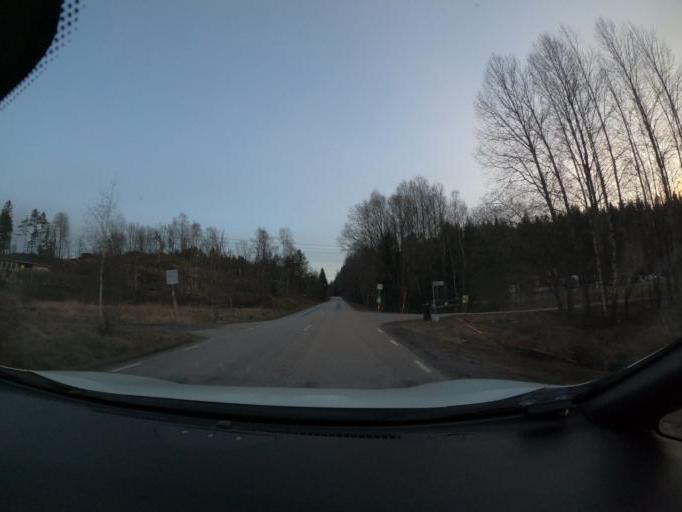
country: SE
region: Vaestra Goetaland
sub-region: Harryda Kommun
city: Molnlycke
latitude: 57.6178
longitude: 12.1802
